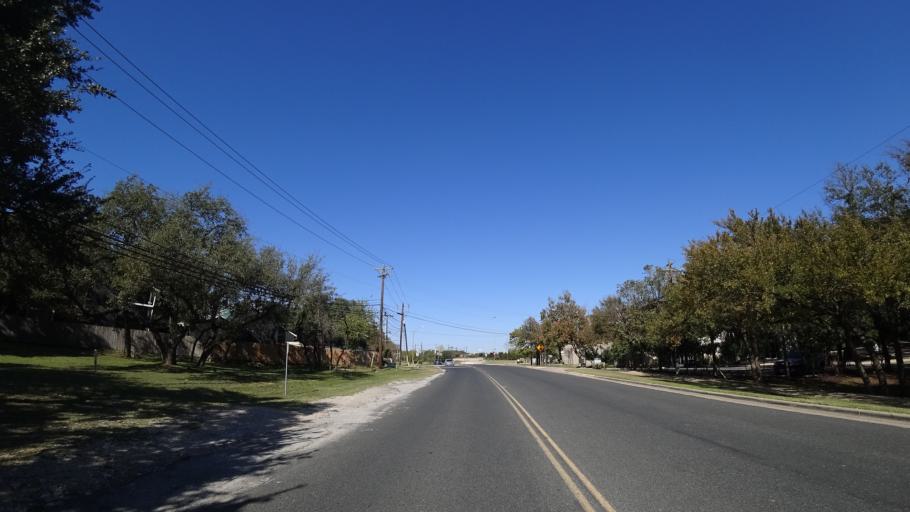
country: US
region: Texas
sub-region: Williamson County
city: Jollyville
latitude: 30.3866
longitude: -97.7455
